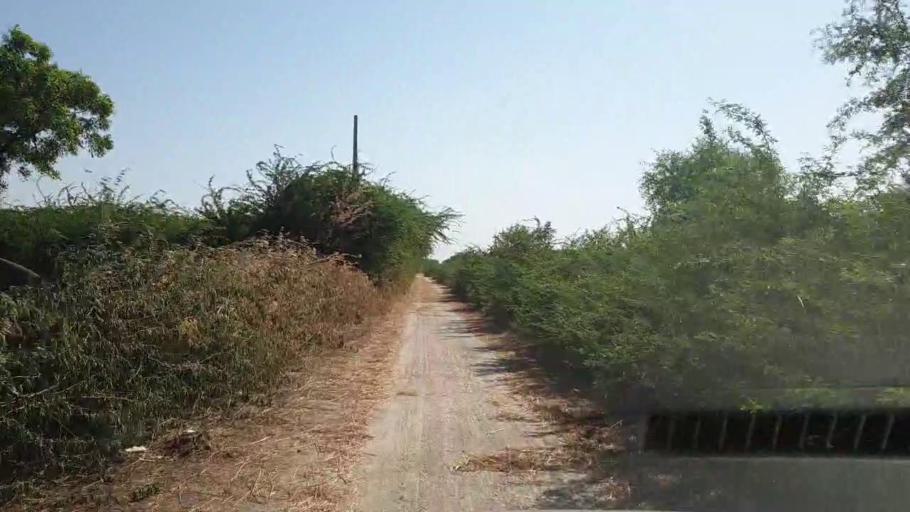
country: PK
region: Sindh
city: Tando Bago
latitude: 24.6365
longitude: 68.9918
